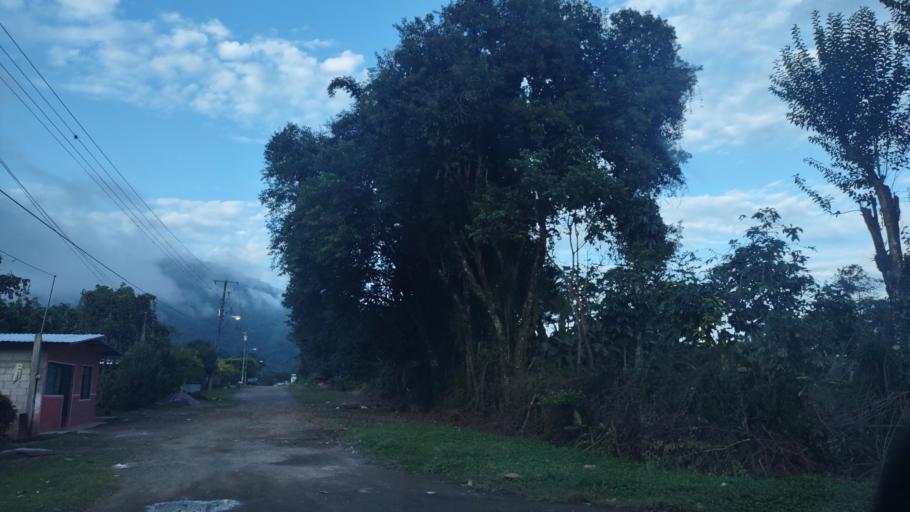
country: MX
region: Veracruz
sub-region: Ixtaczoquitlan
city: Buenavista
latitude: 18.9209
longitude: -97.0449
